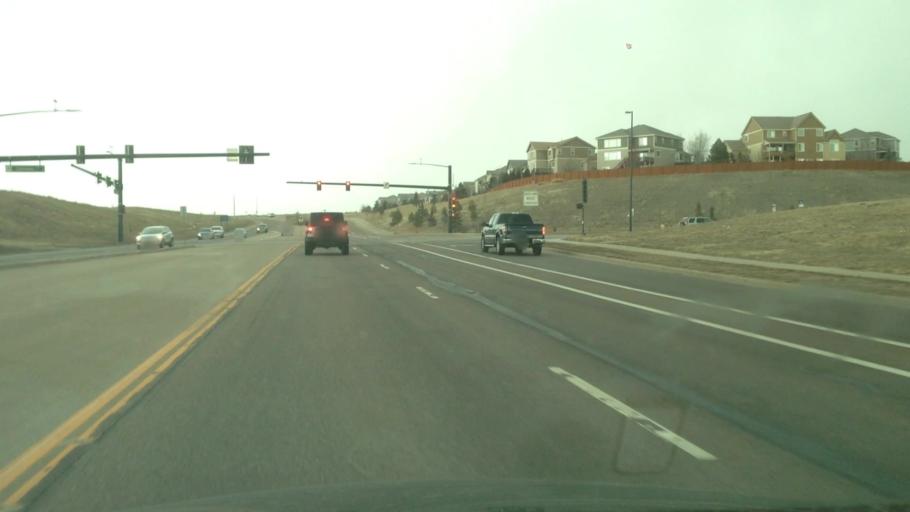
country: US
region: Colorado
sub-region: Douglas County
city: Stonegate
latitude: 39.4930
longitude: -104.8003
